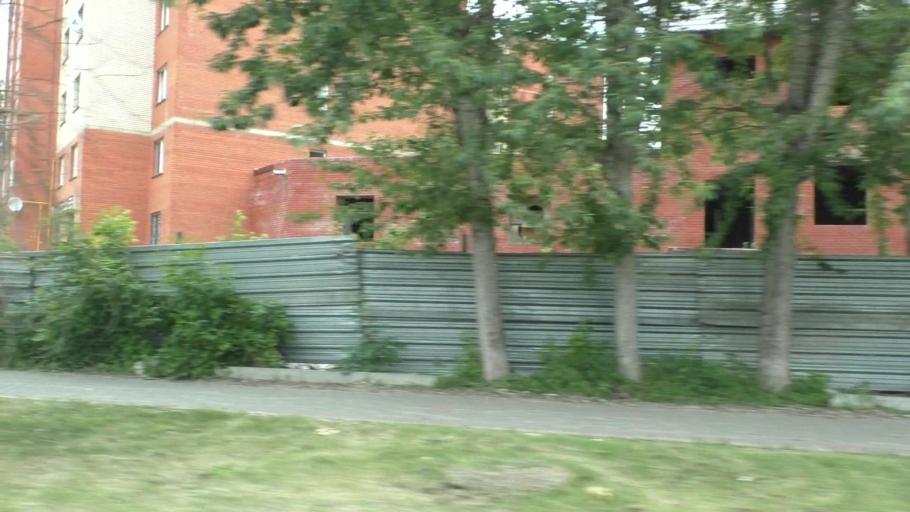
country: RU
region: Moskovskaya
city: Yegor'yevsk
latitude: 55.3677
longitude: 39.0555
